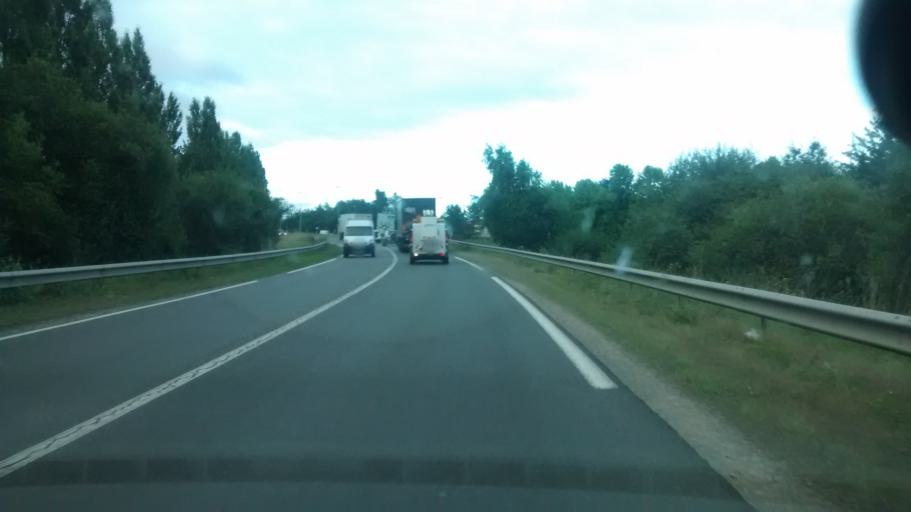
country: FR
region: Brittany
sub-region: Departement d'Ille-et-Vilaine
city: Le Rheu
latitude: 48.0925
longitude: -1.7921
